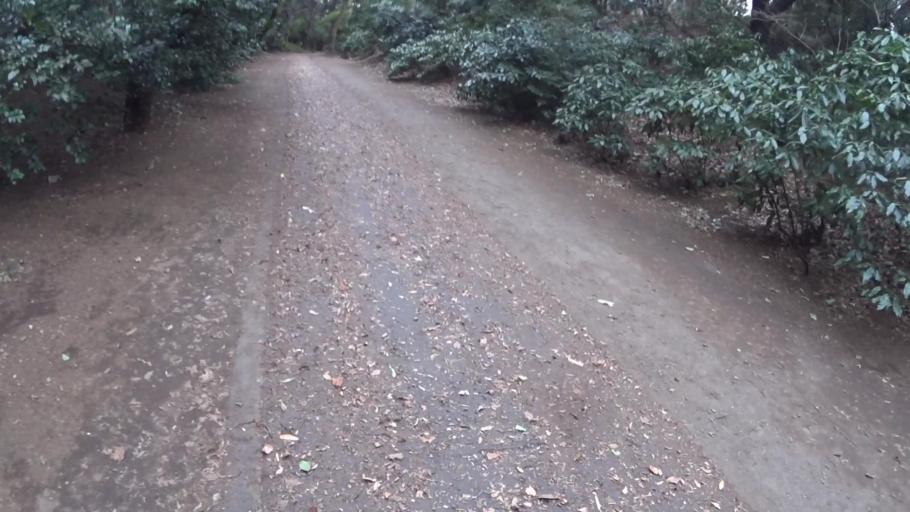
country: JP
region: Tokyo
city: Tokyo
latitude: 35.7339
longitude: 139.7473
